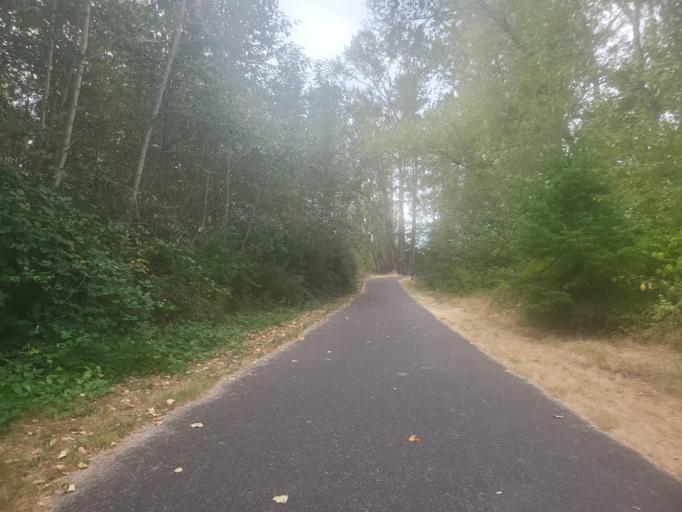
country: US
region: Washington
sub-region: King County
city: Pacific
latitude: 47.2434
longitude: -122.2357
